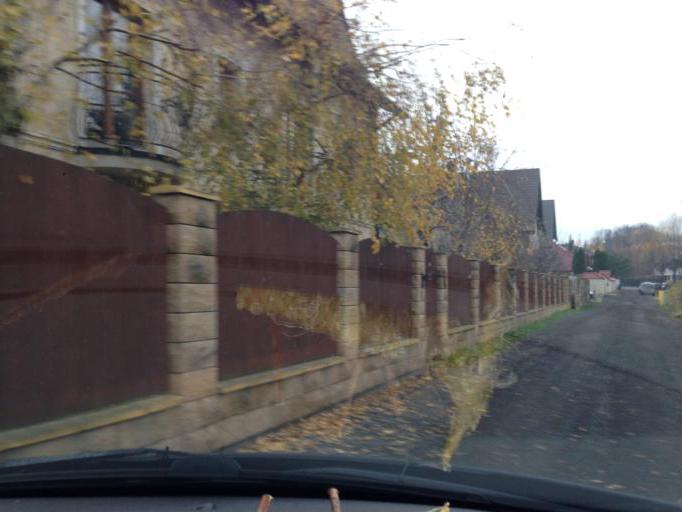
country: PL
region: Lesser Poland Voivodeship
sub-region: Powiat krakowski
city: Wrzasowice
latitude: 50.0027
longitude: 19.9592
